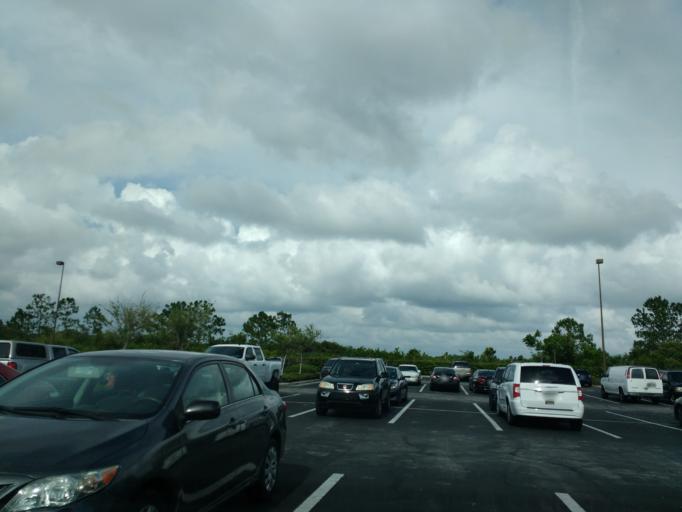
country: US
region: Florida
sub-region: Manatee County
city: Ellenton
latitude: 27.5376
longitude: -82.5080
